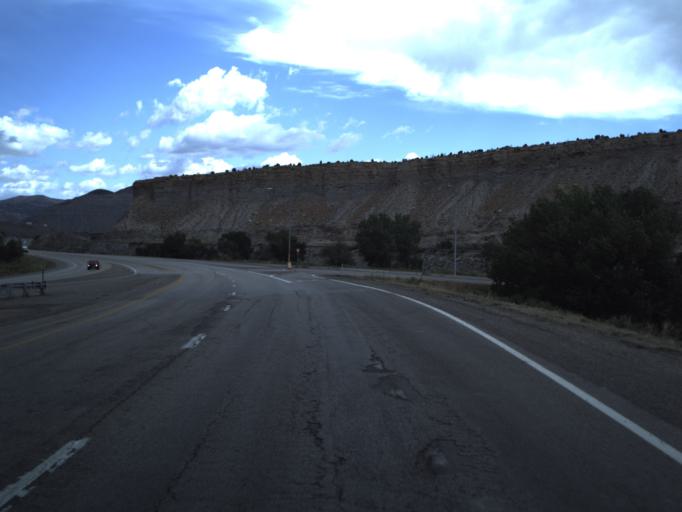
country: US
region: Utah
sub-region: Carbon County
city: Spring Glen
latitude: 39.6397
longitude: -110.8594
